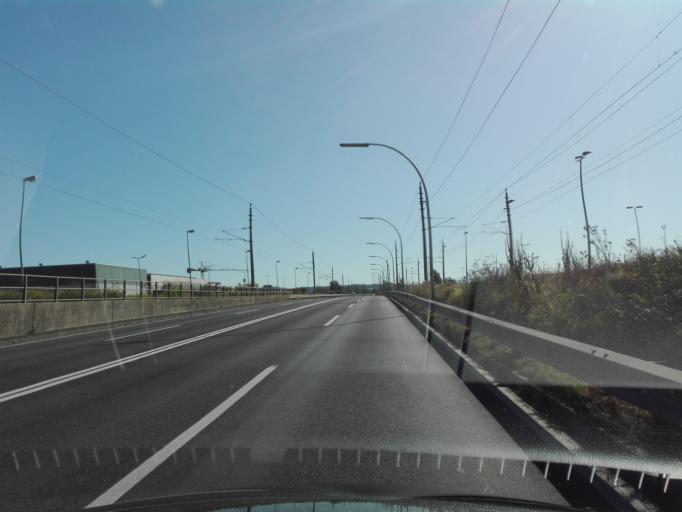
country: AT
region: Upper Austria
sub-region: Linz Stadt
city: Linz
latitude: 48.2709
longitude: 14.3204
